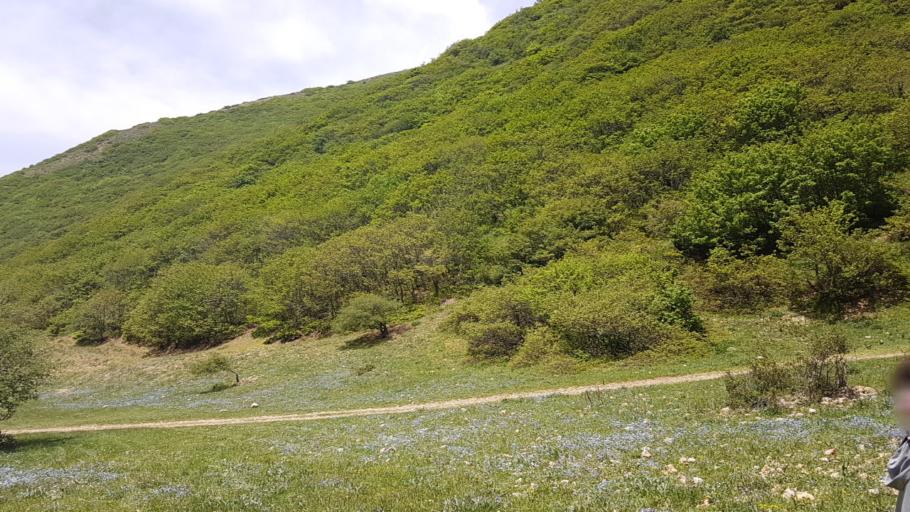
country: IR
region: Ardabil
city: Khalkhal
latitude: 37.6598
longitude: 48.5948
